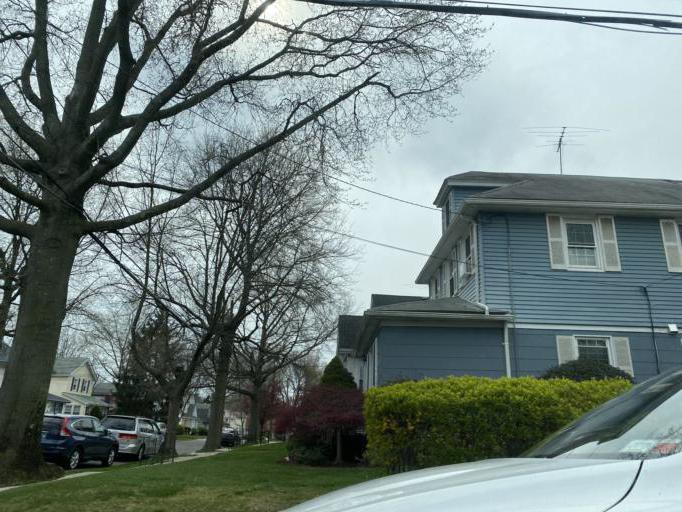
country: US
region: New York
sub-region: Nassau County
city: Floral Park
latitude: 40.7213
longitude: -73.7097
